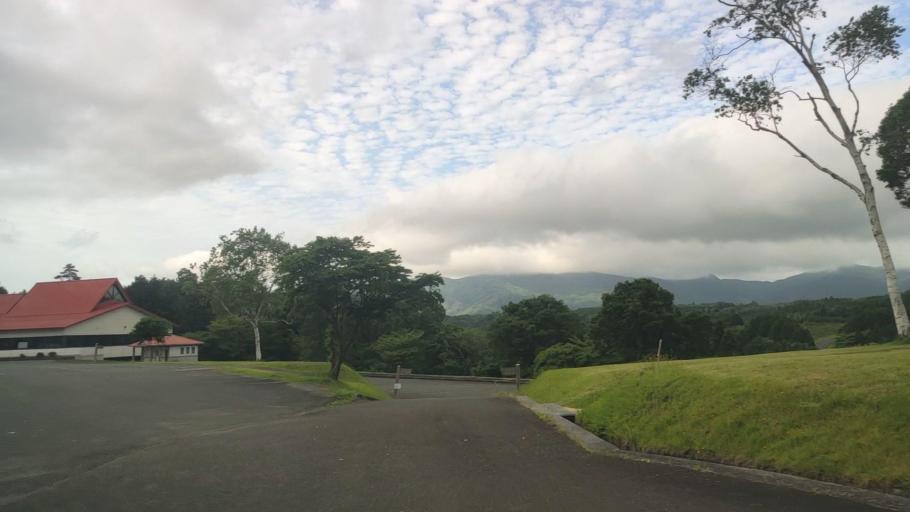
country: JP
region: Tottori
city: Kurayoshi
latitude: 35.2976
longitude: 133.6285
